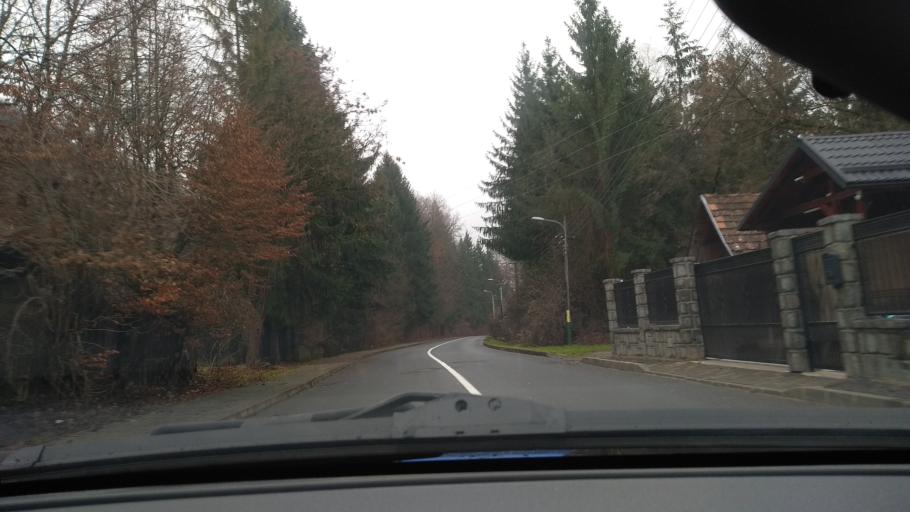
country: RO
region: Mures
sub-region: Oras Sovata
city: Sovata
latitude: 46.5960
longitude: 25.0815
